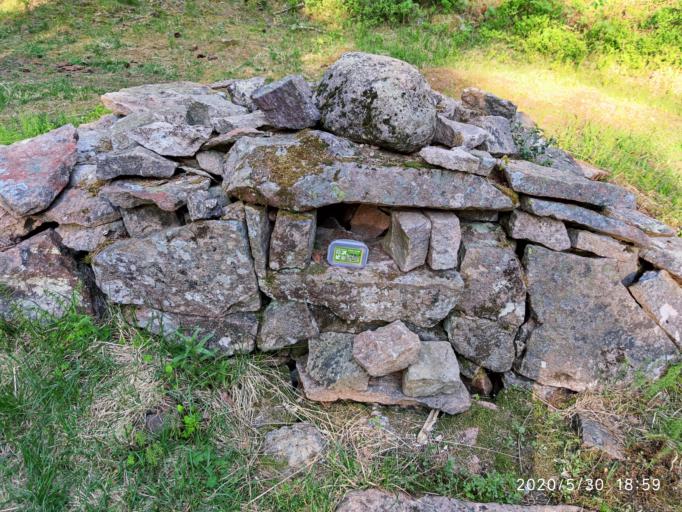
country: NO
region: Buskerud
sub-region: Drammen
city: Drammen
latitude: 59.7601
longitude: 10.1912
